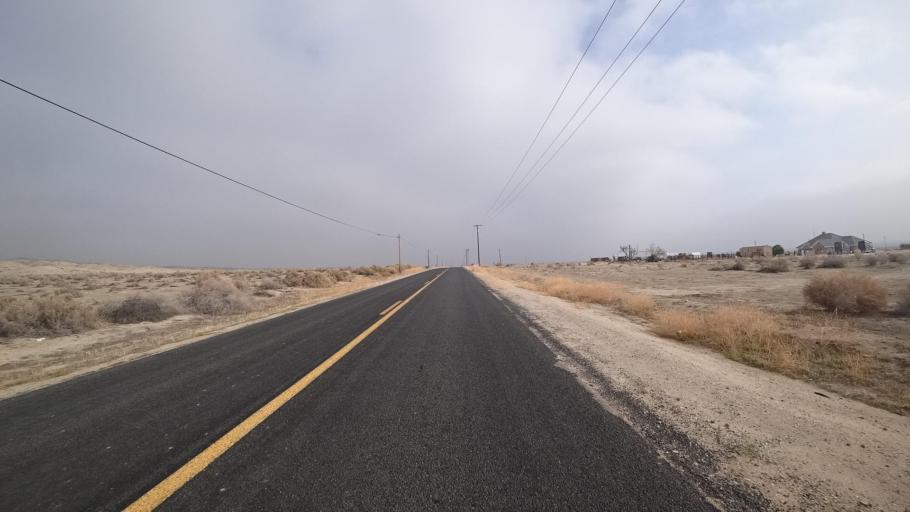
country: US
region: California
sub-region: Kern County
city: Ford City
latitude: 35.2326
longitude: -119.3611
